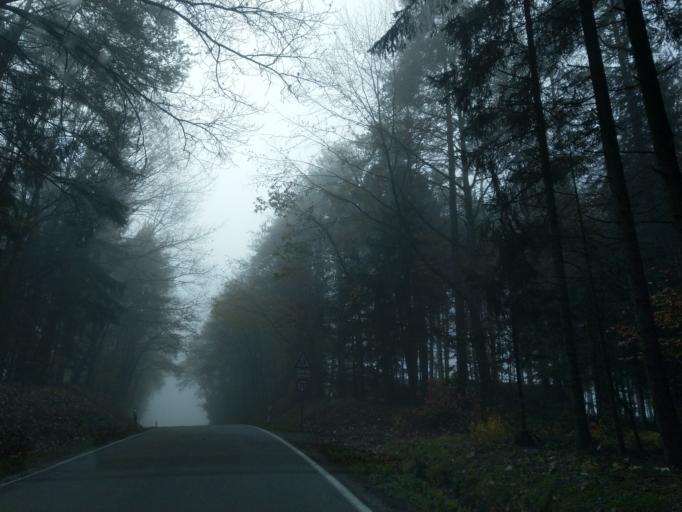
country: DE
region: Bavaria
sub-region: Lower Bavaria
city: Iggensbach
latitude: 48.7675
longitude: 13.1419
